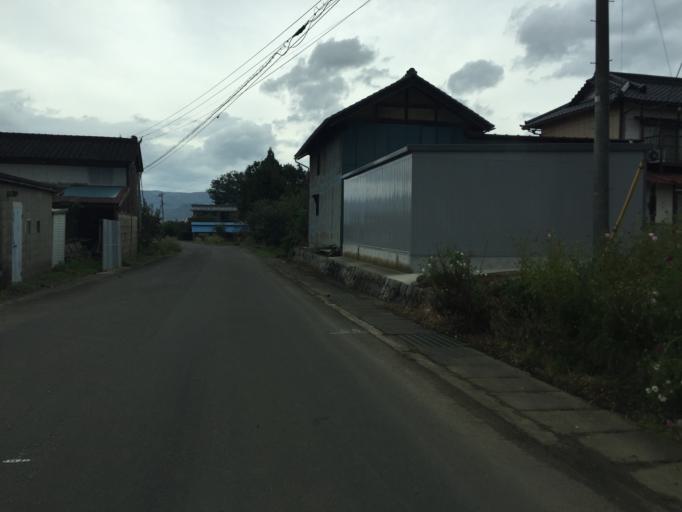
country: JP
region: Fukushima
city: Yanagawamachi-saiwaicho
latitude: 37.8606
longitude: 140.6212
